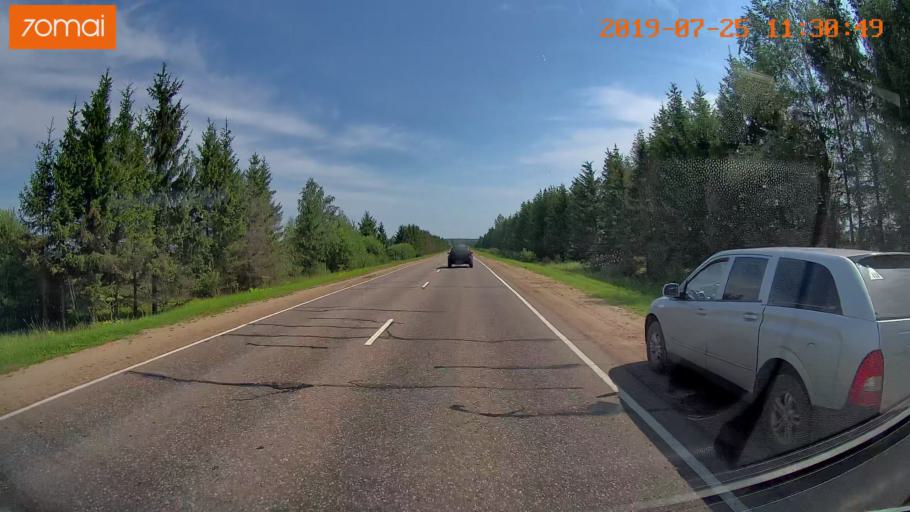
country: RU
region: Ivanovo
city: Privolzhsk
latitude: 57.3871
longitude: 41.3323
